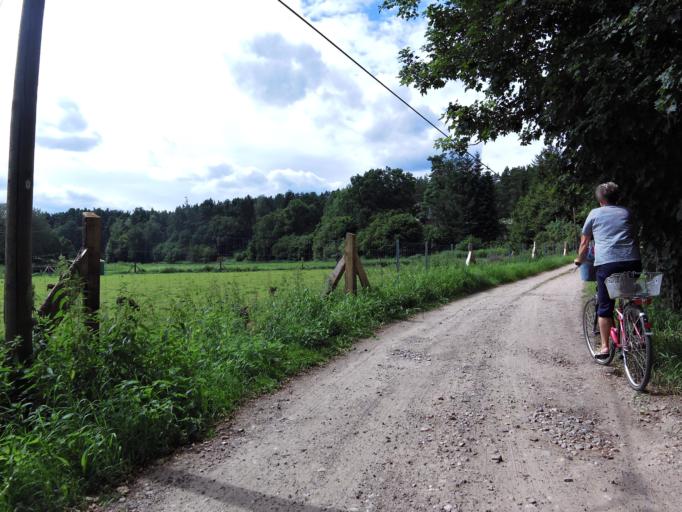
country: DE
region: Brandenburg
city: Lychen
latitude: 53.2193
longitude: 13.2796
